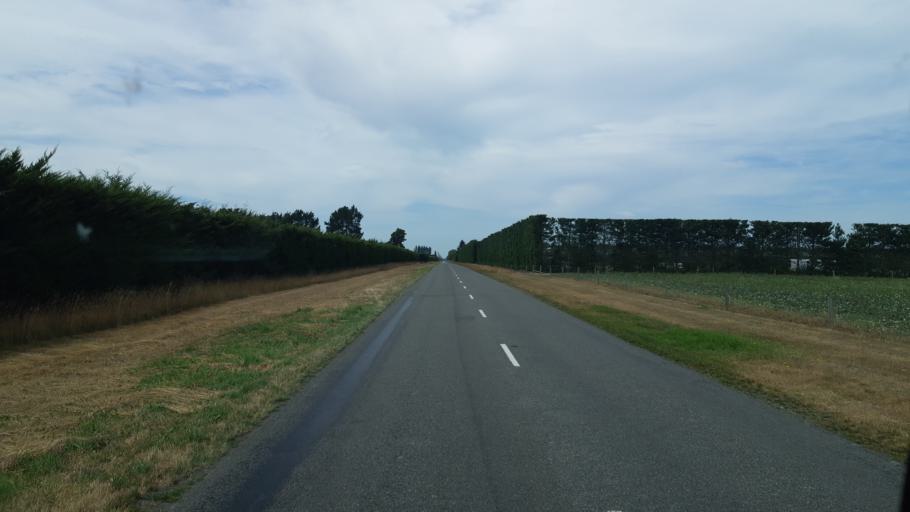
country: NZ
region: Canterbury
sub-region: Ashburton District
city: Tinwald
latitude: -43.9302
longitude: 171.5975
